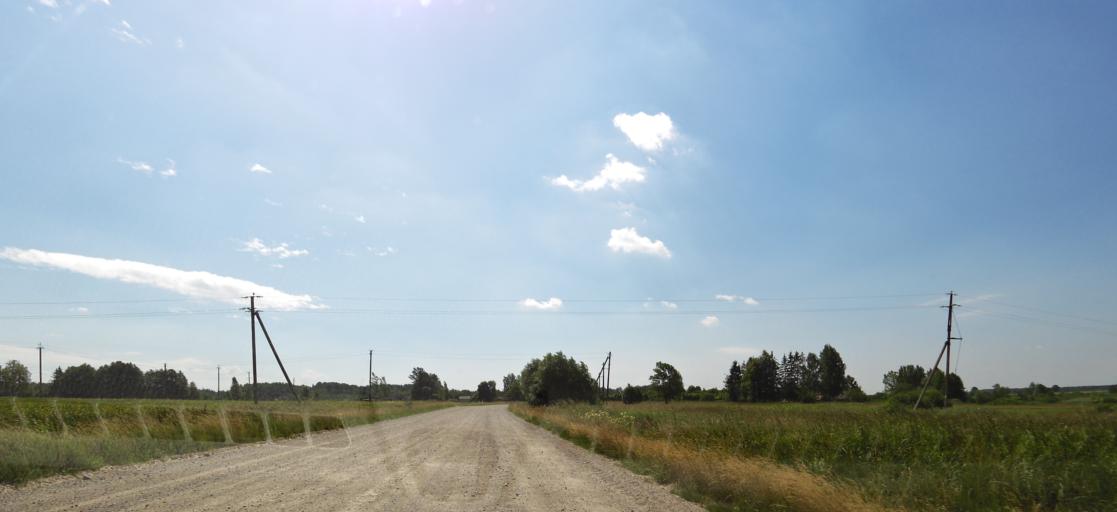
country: LT
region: Panevezys
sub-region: Birzai
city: Birzai
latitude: 56.1911
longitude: 24.9328
